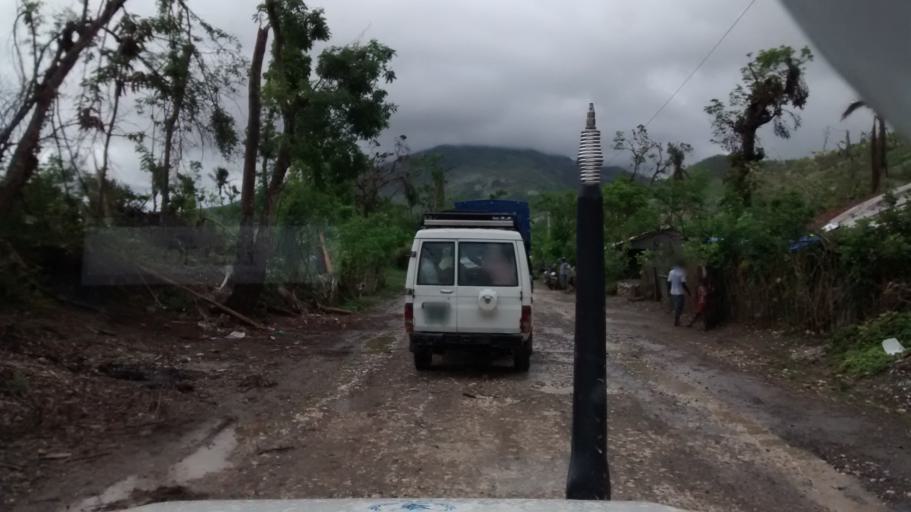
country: HT
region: Grandans
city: Moron
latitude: 18.5987
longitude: -74.1926
